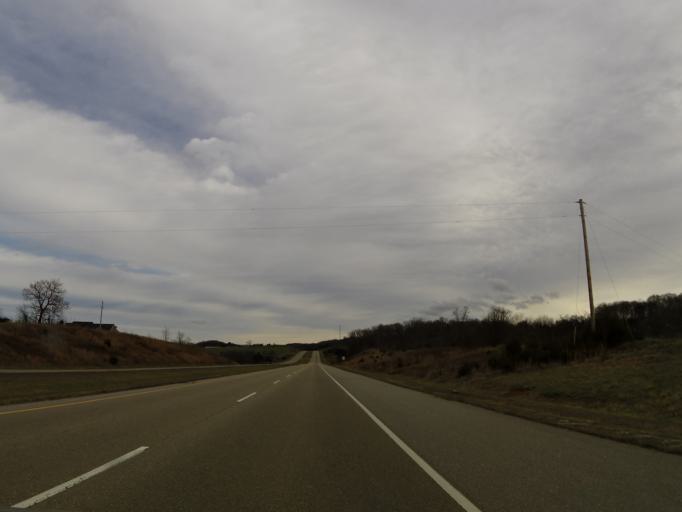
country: US
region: Tennessee
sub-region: Cocke County
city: Newport
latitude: 36.0130
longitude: -83.0544
